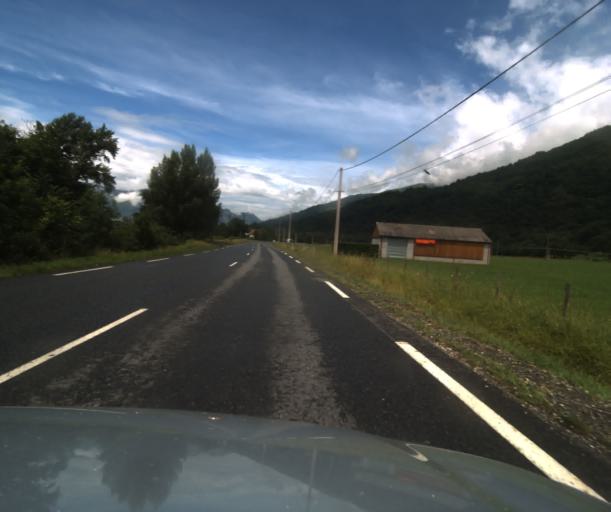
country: FR
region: Midi-Pyrenees
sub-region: Departement des Hautes-Pyrenees
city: Pierrefitte-Nestalas
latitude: 42.9602
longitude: -0.0629
